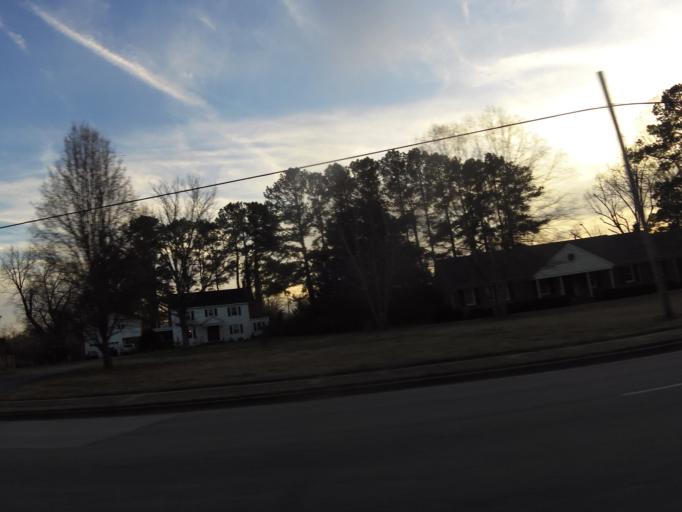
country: US
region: Virginia
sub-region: City of Franklin
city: Franklin
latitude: 36.6820
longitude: -76.9553
